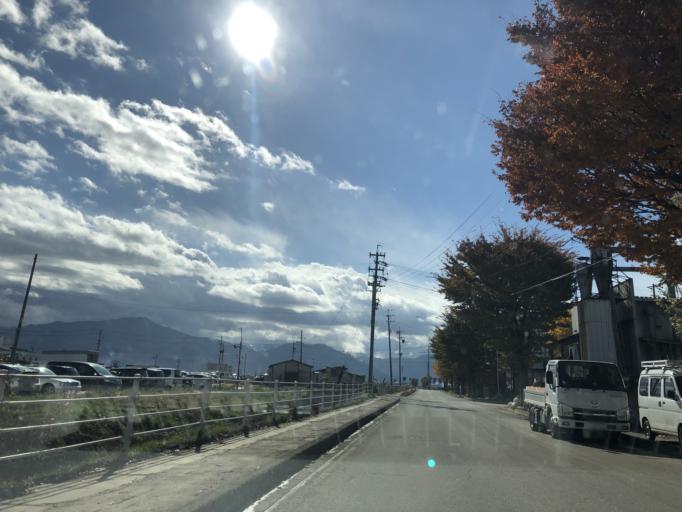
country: JP
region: Nagano
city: Suzaka
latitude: 36.6847
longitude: 138.2615
